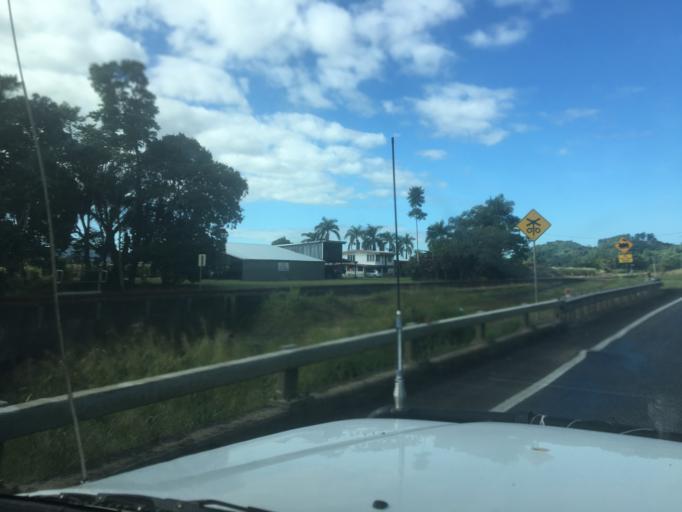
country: AU
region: Queensland
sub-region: Cassowary Coast
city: Innisfail
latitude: -17.2775
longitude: 145.9215
